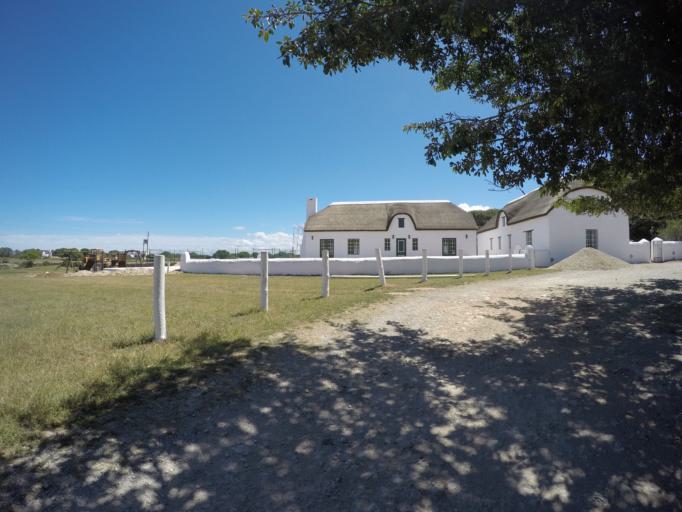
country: ZA
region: Western Cape
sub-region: Overberg District Municipality
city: Bredasdorp
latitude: -34.4552
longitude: 20.3995
